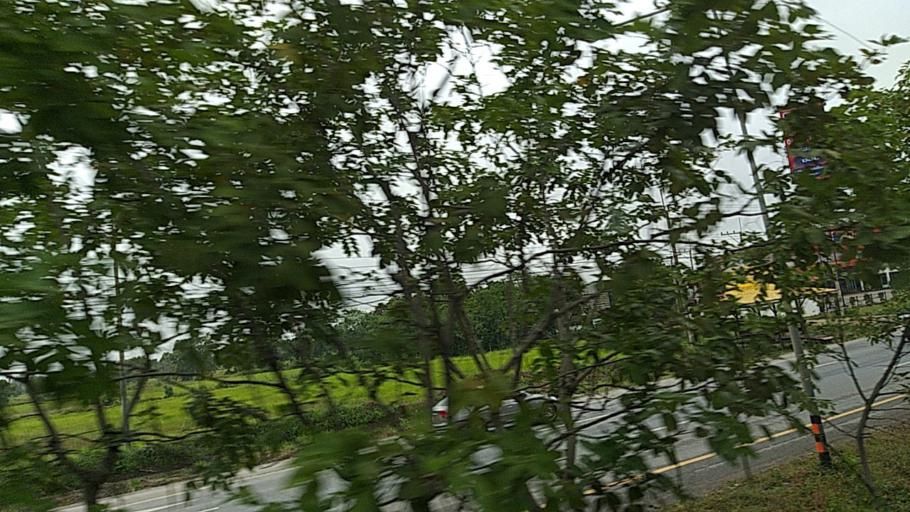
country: TH
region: Nakhon Ratchasima
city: Non Sung
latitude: 15.0944
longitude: 102.2510
